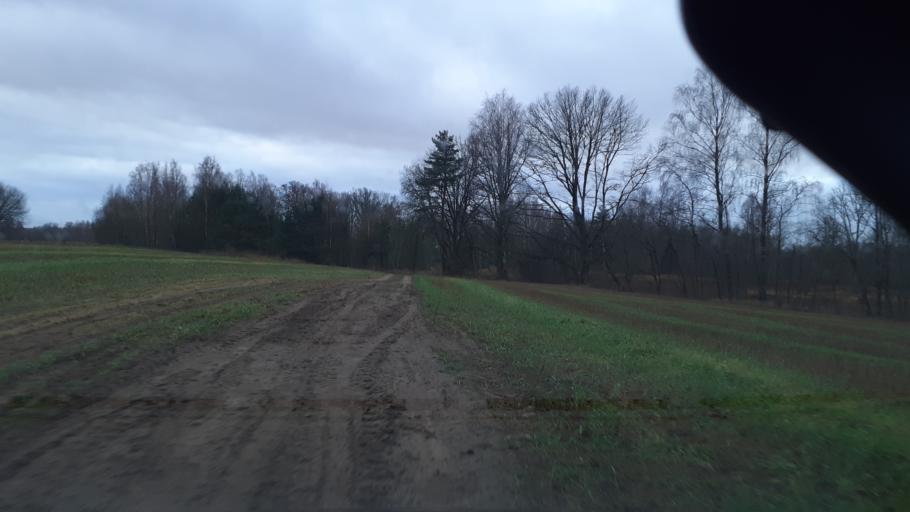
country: LV
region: Kuldigas Rajons
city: Kuldiga
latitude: 56.8809
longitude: 21.7706
